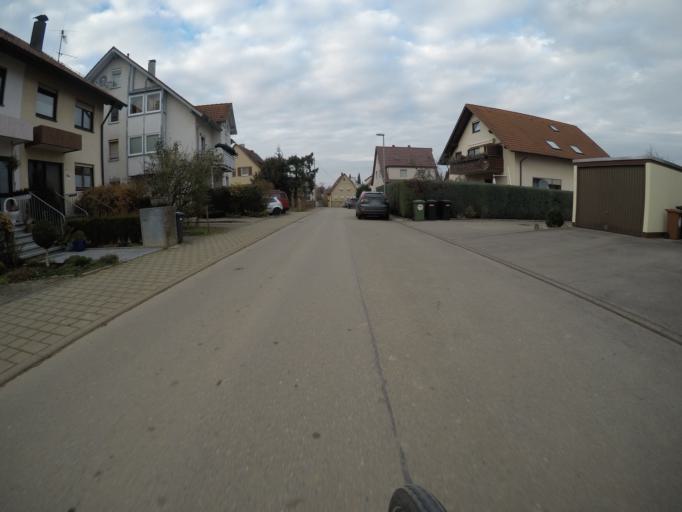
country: DE
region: Baden-Wuerttemberg
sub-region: Regierungsbezirk Stuttgart
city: Leinfelden-Echterdingen
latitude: 48.7007
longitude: 9.2071
